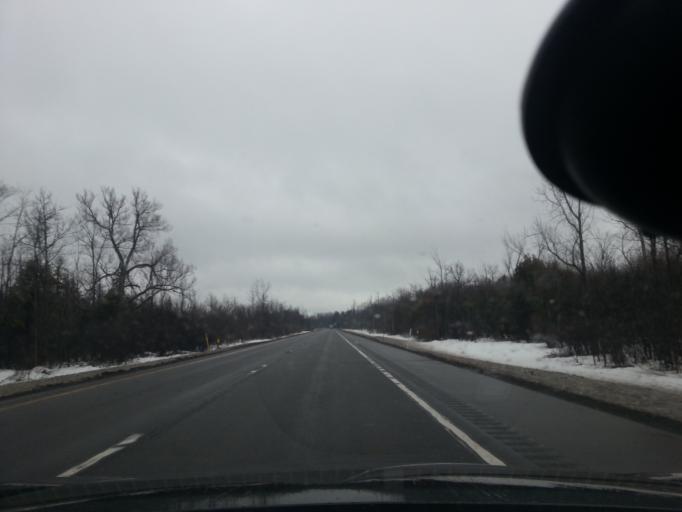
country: US
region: New York
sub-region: Jefferson County
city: Adams
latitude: 43.8365
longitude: -76.0276
